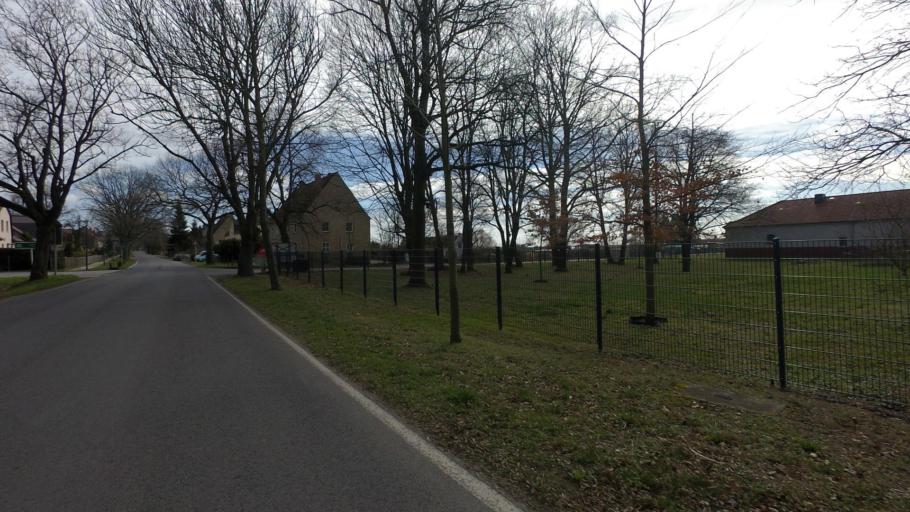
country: DE
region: Berlin
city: Blankenfelde
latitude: 52.6580
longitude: 13.4239
